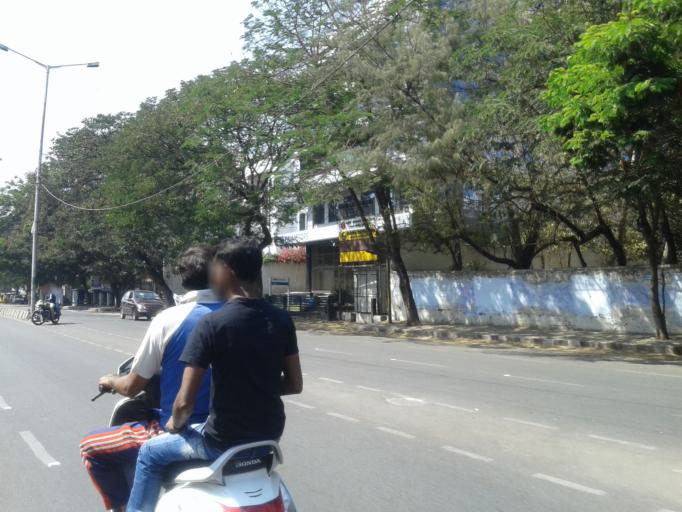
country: IN
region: Telangana
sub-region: Hyderabad
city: Hyderabad
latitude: 17.4011
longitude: 78.4726
